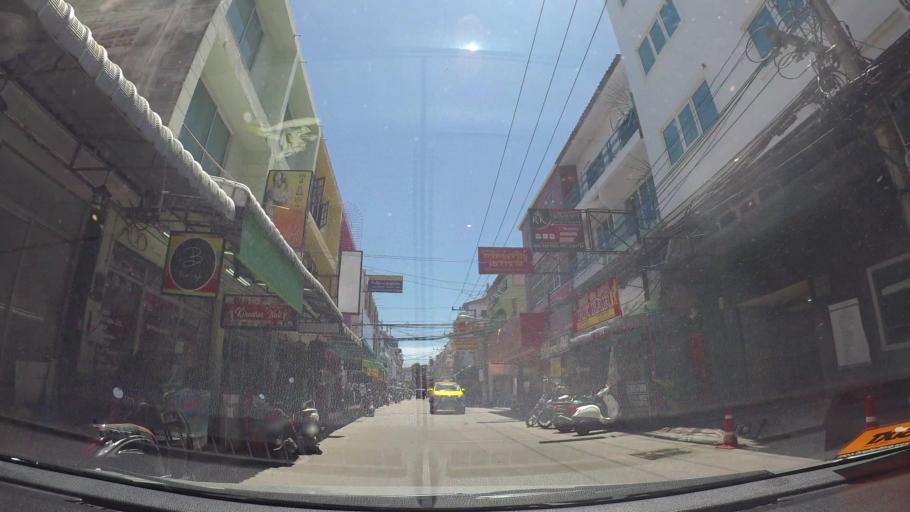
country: TH
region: Chon Buri
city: Phatthaya
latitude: 12.9231
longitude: 100.8773
